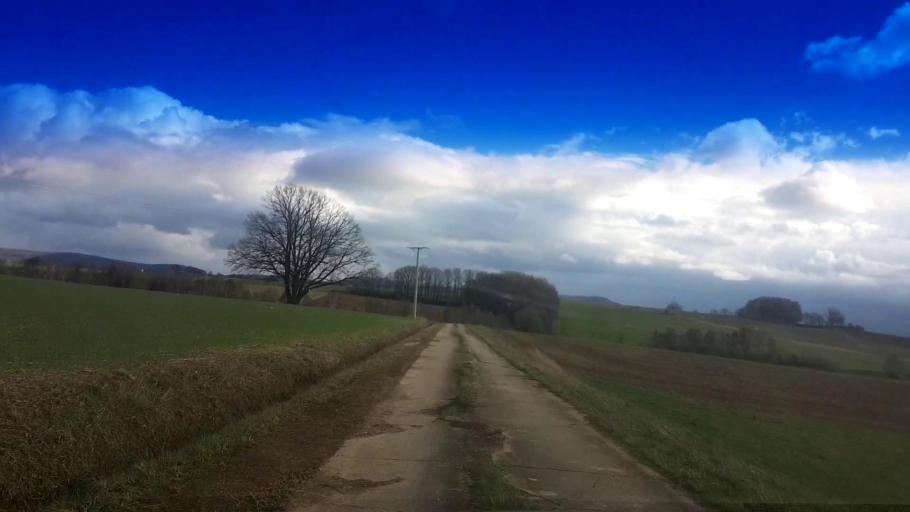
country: DE
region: Bavaria
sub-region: Upper Franconia
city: Schesslitz
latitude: 49.9922
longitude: 11.0173
